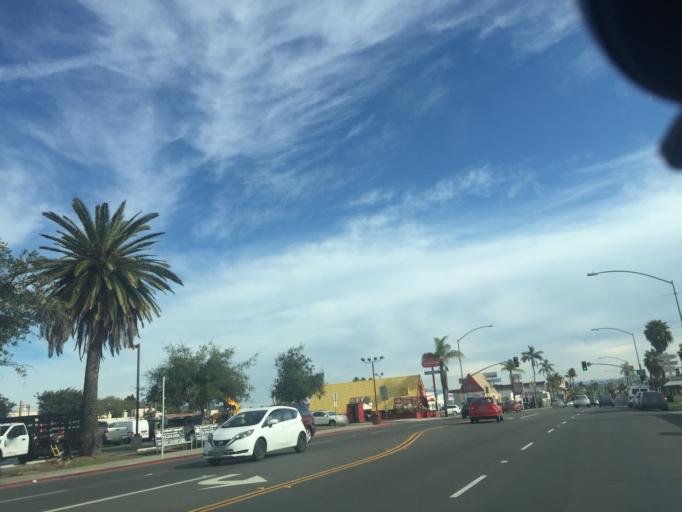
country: US
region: California
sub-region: San Diego County
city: Lemon Grove
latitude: 32.7553
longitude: -117.0975
